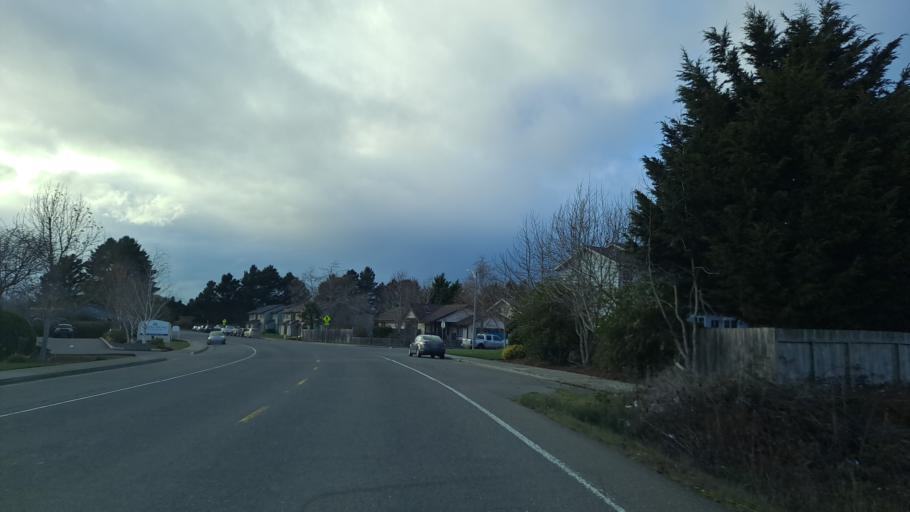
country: US
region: California
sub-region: Humboldt County
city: Fortuna
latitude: 40.5845
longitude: -124.1390
